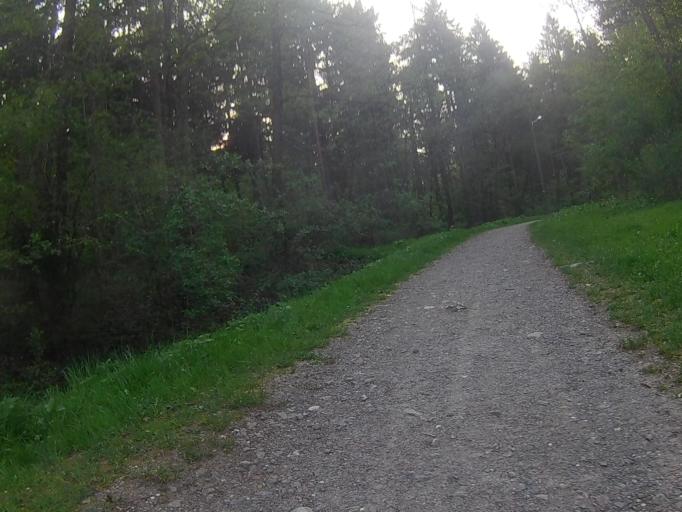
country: SI
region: Maribor
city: Pekre
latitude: 46.5337
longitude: 15.5976
